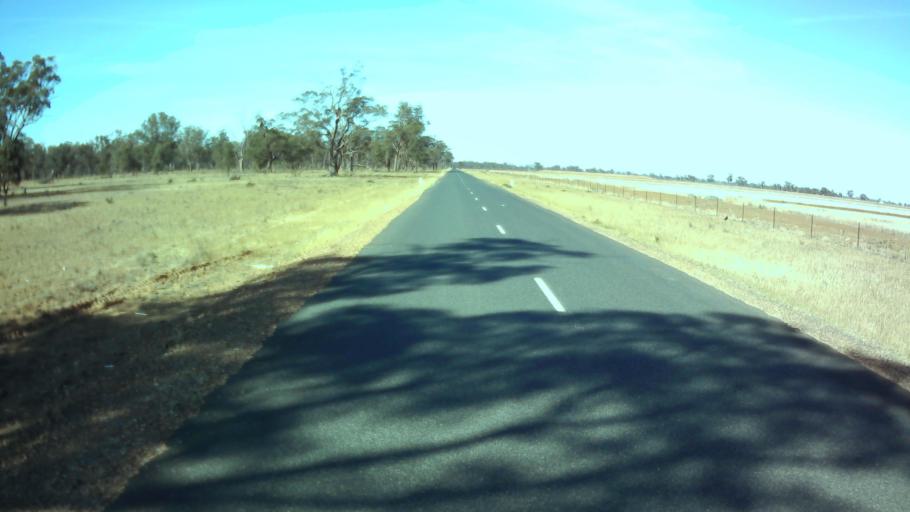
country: AU
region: New South Wales
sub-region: Weddin
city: Grenfell
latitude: -34.1211
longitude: 147.8109
